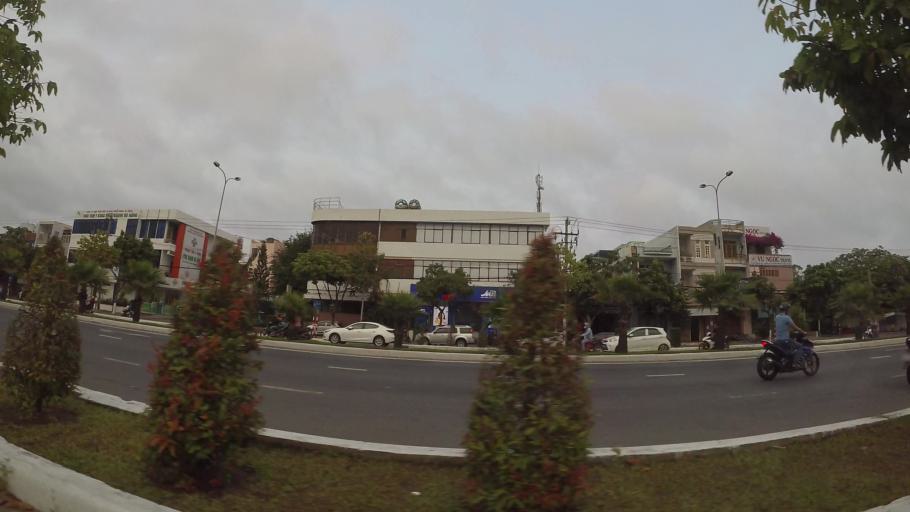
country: VN
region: Da Nang
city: Son Tra
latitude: 16.0575
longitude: 108.2355
